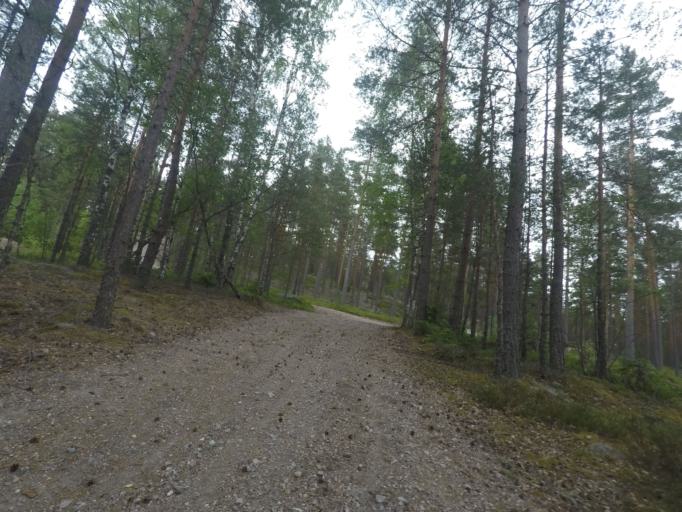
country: SE
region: Vaestmanland
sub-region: Kungsors Kommun
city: Kungsoer
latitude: 59.3709
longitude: 16.1063
